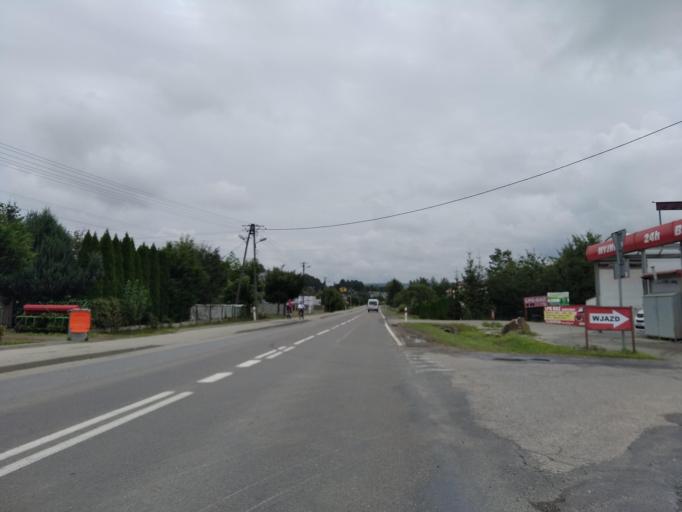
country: PL
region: Subcarpathian Voivodeship
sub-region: Powiat przemyski
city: Bircza
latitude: 49.6907
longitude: 22.4620
